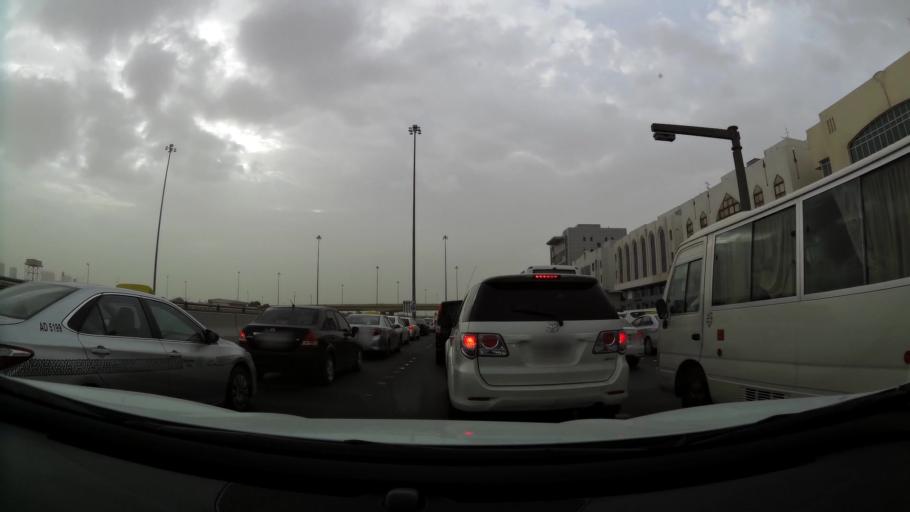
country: AE
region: Abu Dhabi
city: Abu Dhabi
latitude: 24.4826
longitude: 54.3848
